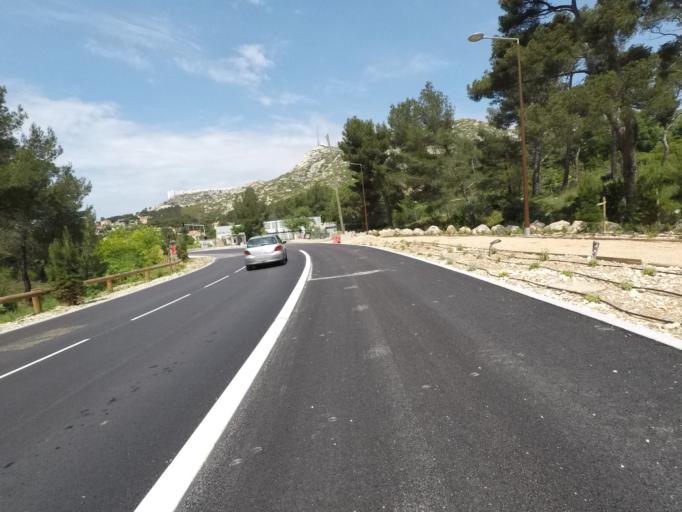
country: FR
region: Provence-Alpes-Cote d'Azur
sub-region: Departement des Bouches-du-Rhone
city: Marseille 09
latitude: 43.2459
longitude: 5.4372
